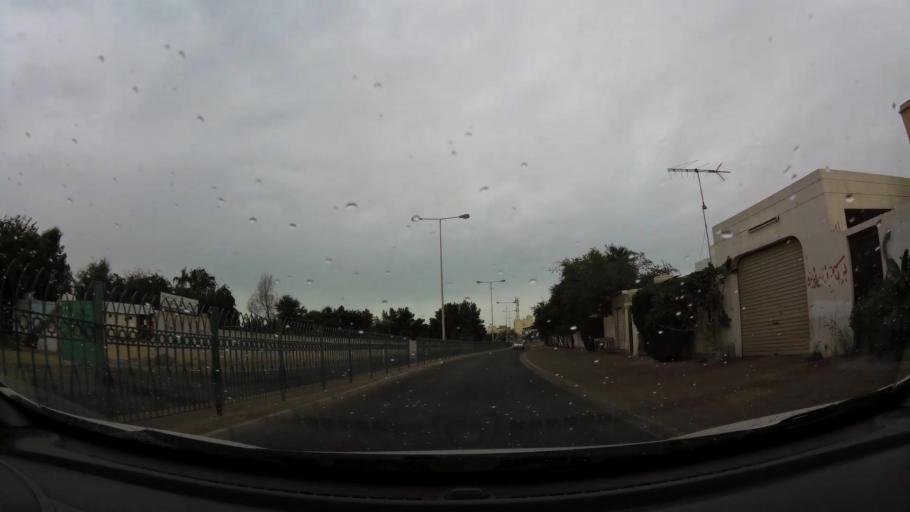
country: BH
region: Central Governorate
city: Madinat Hamad
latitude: 26.1109
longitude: 50.4824
